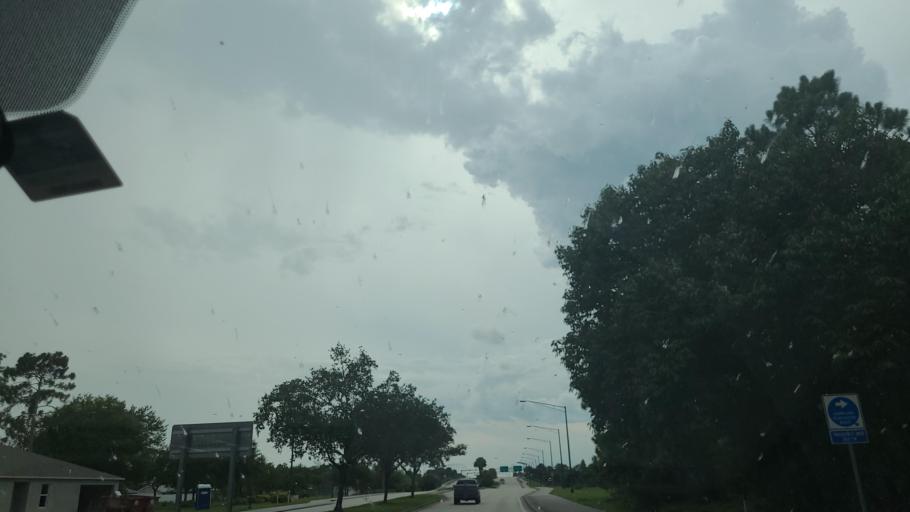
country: US
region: Florida
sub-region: Saint Lucie County
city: Port Saint Lucie
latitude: 27.2098
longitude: -80.3933
